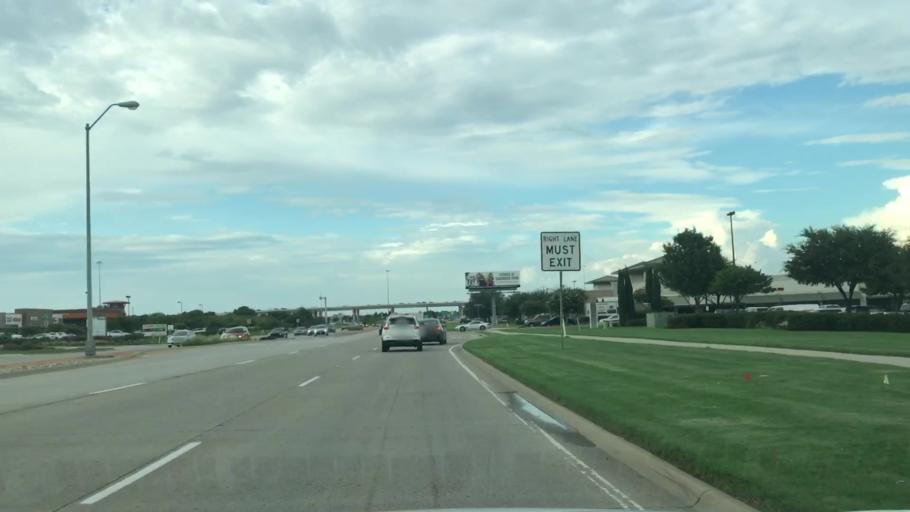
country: US
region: Texas
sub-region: Collin County
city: Frisco
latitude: 33.0901
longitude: -96.8054
